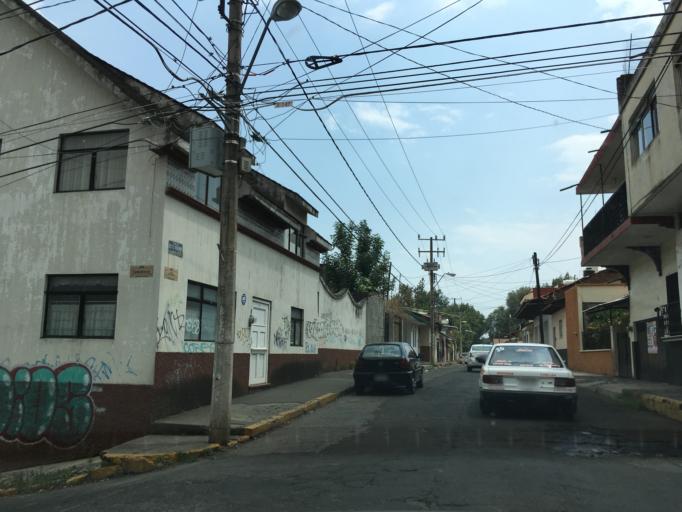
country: MX
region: Michoacan
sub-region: Uruapan
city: Uruapan
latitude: 19.4193
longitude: -102.0656
